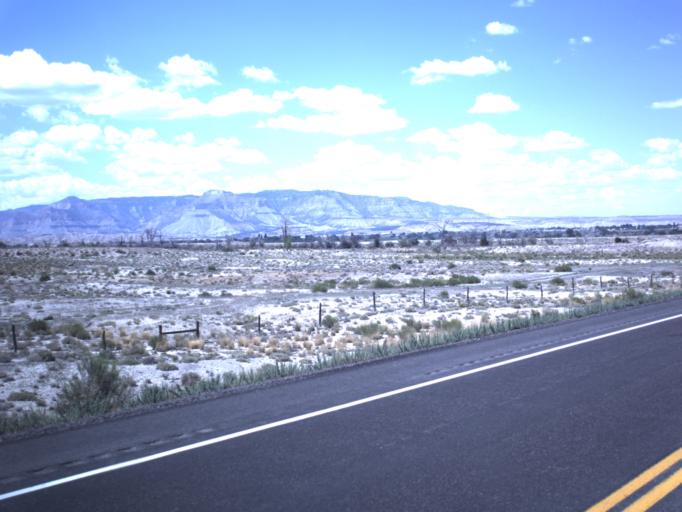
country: US
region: Utah
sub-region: Emery County
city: Huntington
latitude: 39.2835
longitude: -110.9739
